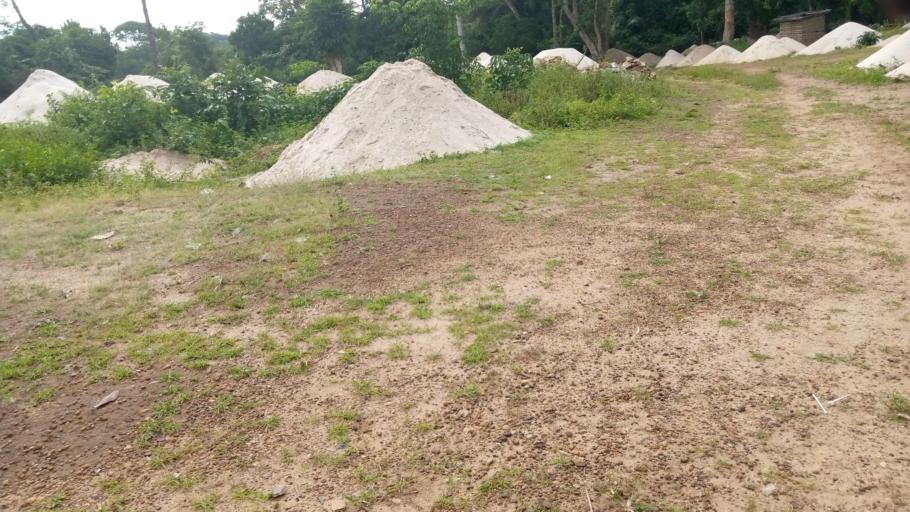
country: SL
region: Southern Province
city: Pujehun
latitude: 7.3485
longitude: -11.7174
